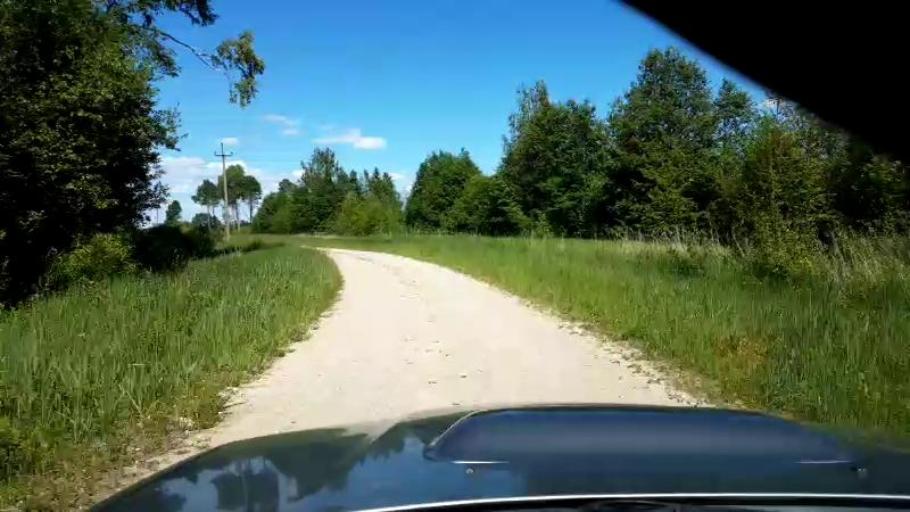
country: EE
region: Paernumaa
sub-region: Halinga vald
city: Parnu-Jaagupi
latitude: 58.5262
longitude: 24.5251
